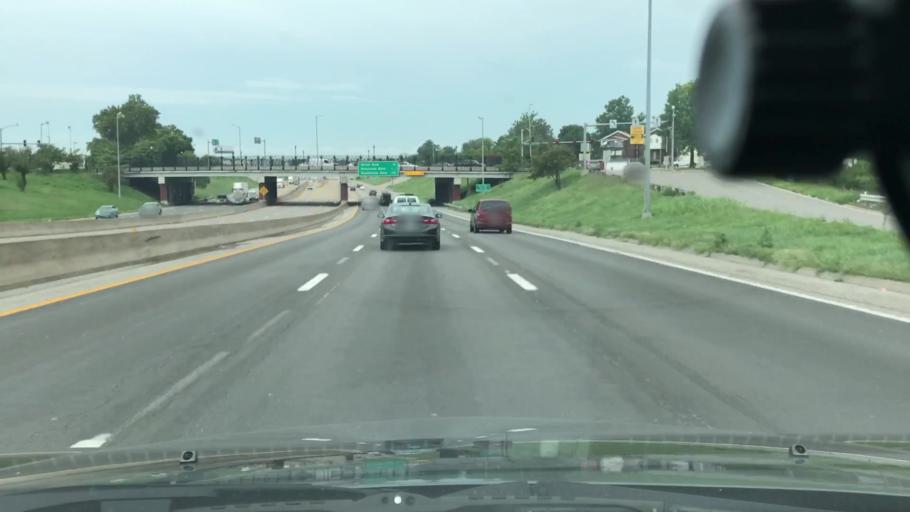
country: US
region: Missouri
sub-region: Saint Louis County
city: Pine Lawn
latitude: 38.6856
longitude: -90.2440
